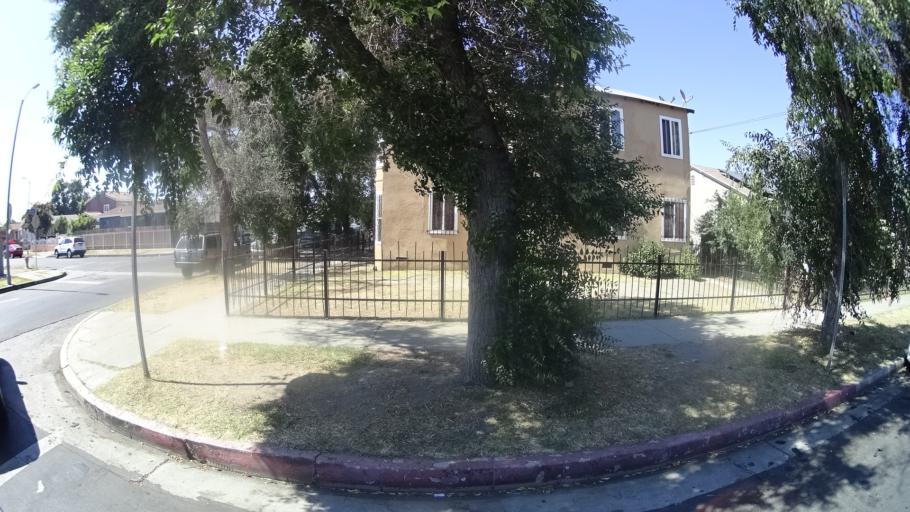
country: US
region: California
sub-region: Los Angeles County
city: Westmont
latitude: 33.9897
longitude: -118.2957
